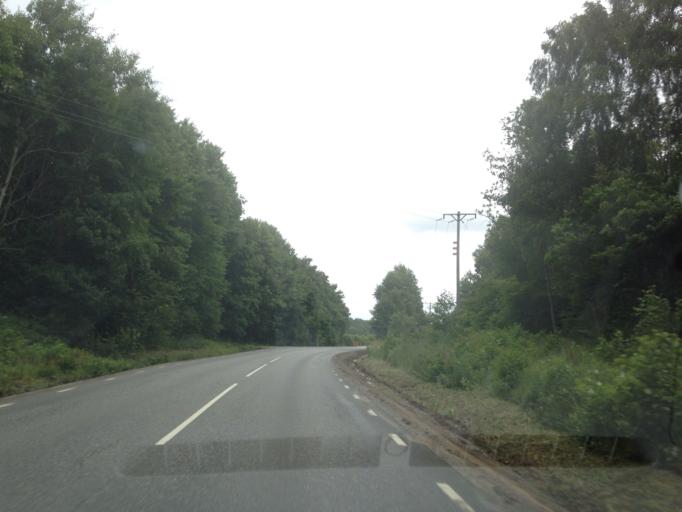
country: SE
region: Vaestra Goetaland
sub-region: Kungalvs Kommun
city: Kode
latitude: 57.8575
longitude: 11.8545
